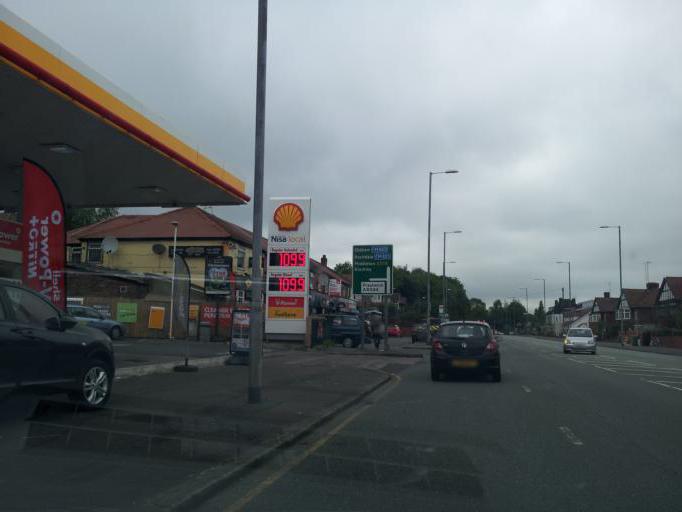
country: GB
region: England
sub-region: Manchester
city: Crumpsall
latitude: 53.5277
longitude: -2.2472
